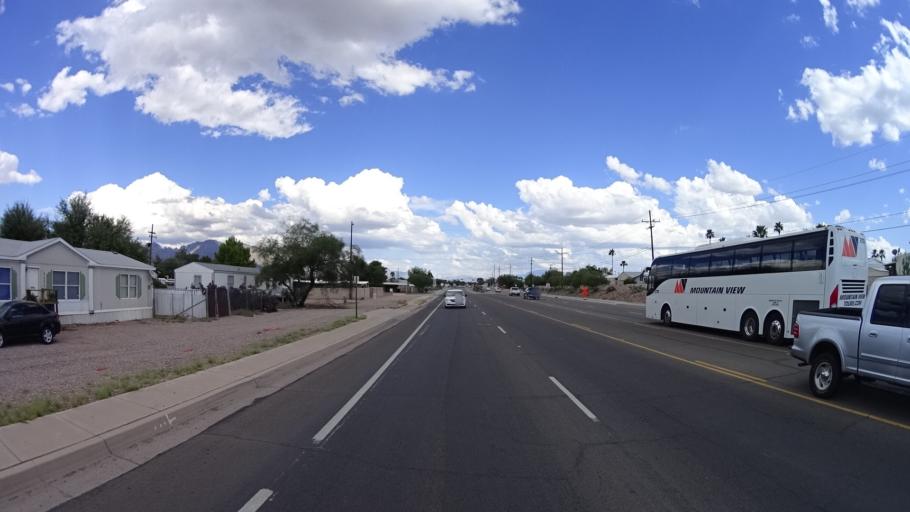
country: US
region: Arizona
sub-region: Pima County
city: Flowing Wells
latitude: 32.2944
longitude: -111.0159
